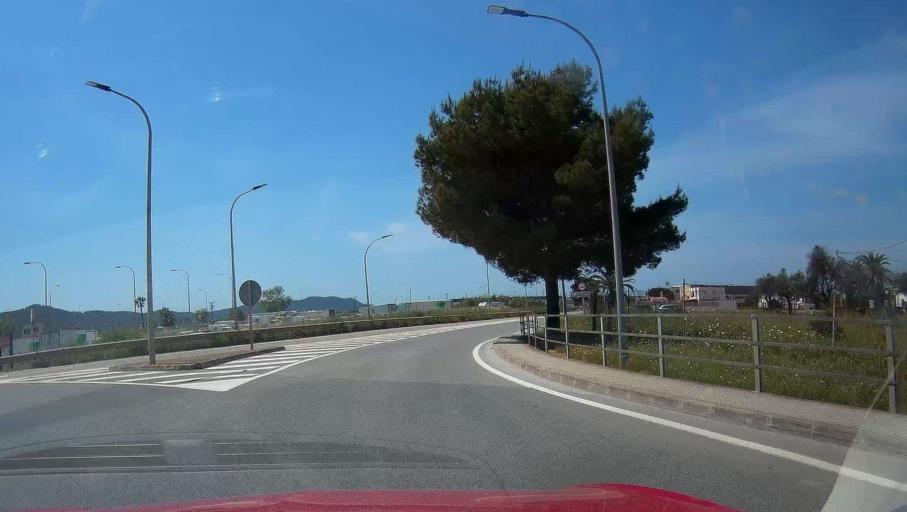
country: ES
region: Balearic Islands
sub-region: Illes Balears
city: Ibiza
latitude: 38.8880
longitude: 1.3955
